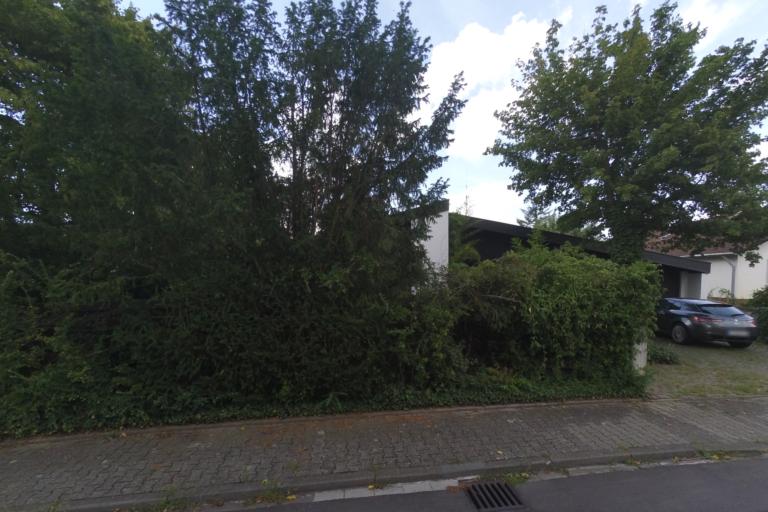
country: DE
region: Rheinland-Pfalz
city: Limburgerhof
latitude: 49.4164
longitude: 8.3854
